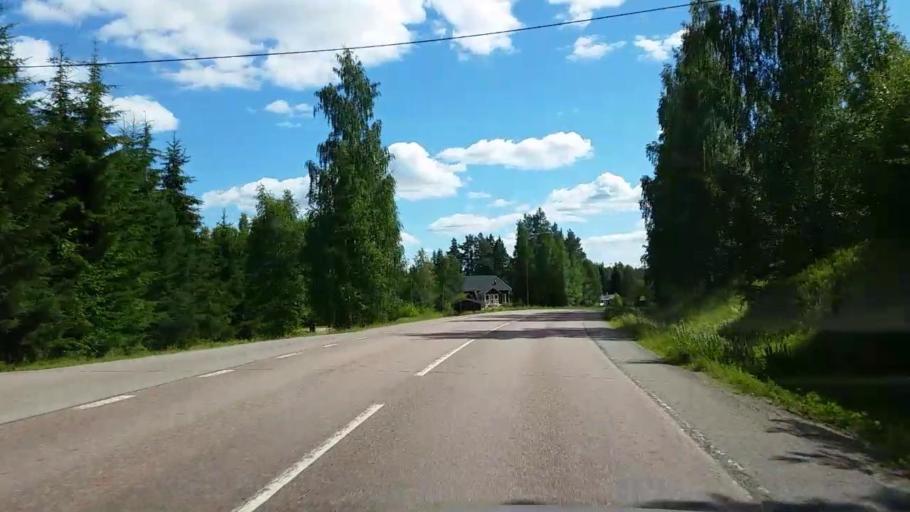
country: SE
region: Dalarna
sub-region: Faluns Kommun
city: Svardsjo
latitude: 60.8272
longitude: 15.7609
